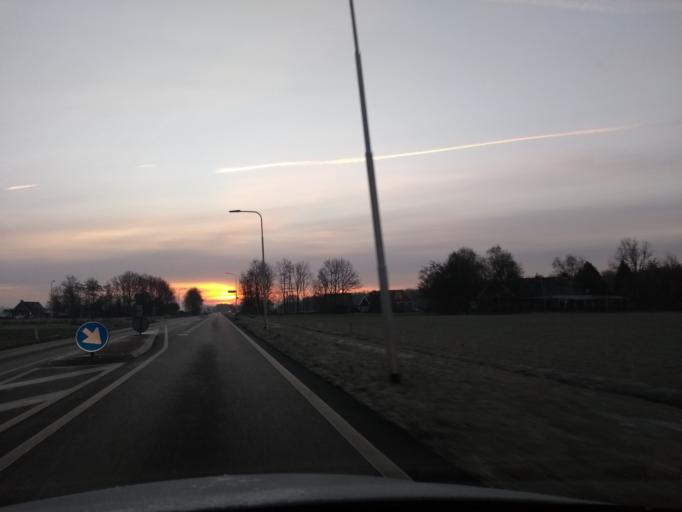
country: NL
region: Friesland
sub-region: Gemeente Gaasterlan-Sleat
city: Balk
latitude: 52.8839
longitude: 5.5979
